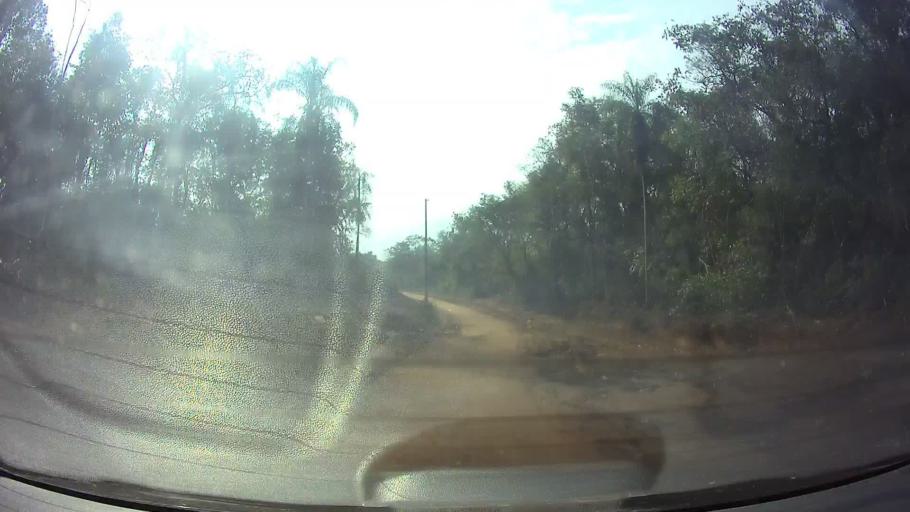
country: PY
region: Cordillera
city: Arroyos y Esteros
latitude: -25.0162
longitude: -57.1967
